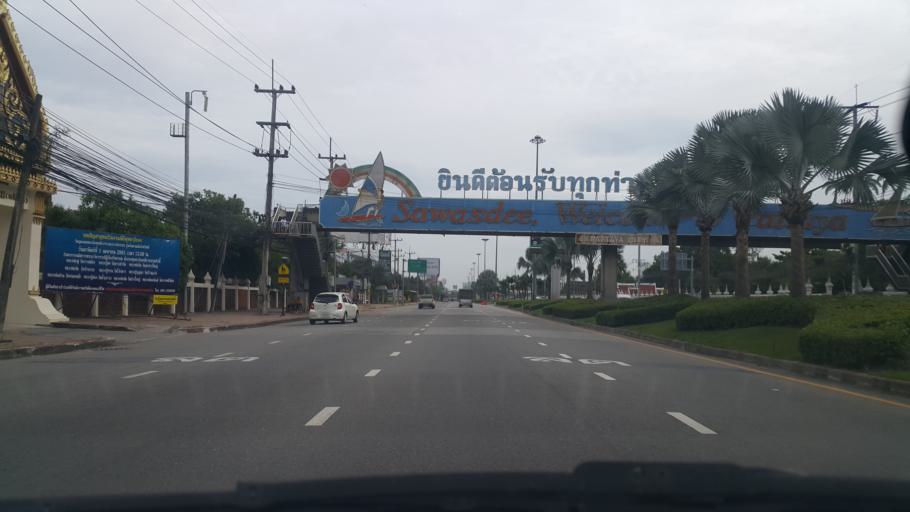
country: TH
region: Chon Buri
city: Bang Lamung
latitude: 12.9959
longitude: 100.9279
